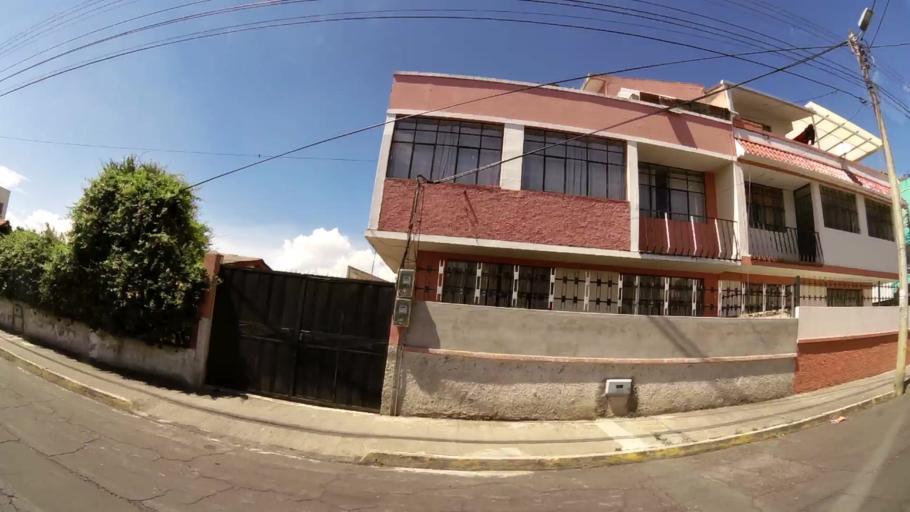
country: EC
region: Chimborazo
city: Riobamba
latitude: -1.6735
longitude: -78.6367
